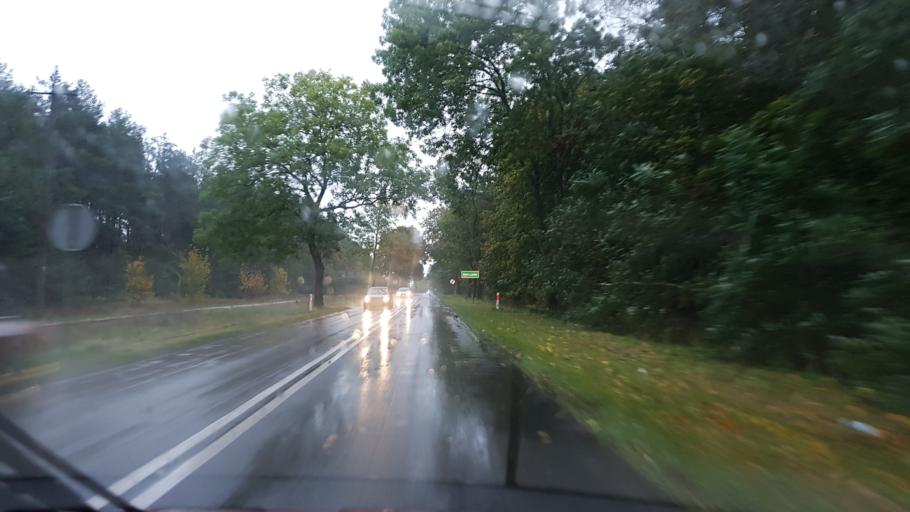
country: PL
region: Greater Poland Voivodeship
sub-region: Powiat pilski
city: Szydlowo
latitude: 53.1566
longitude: 16.6707
